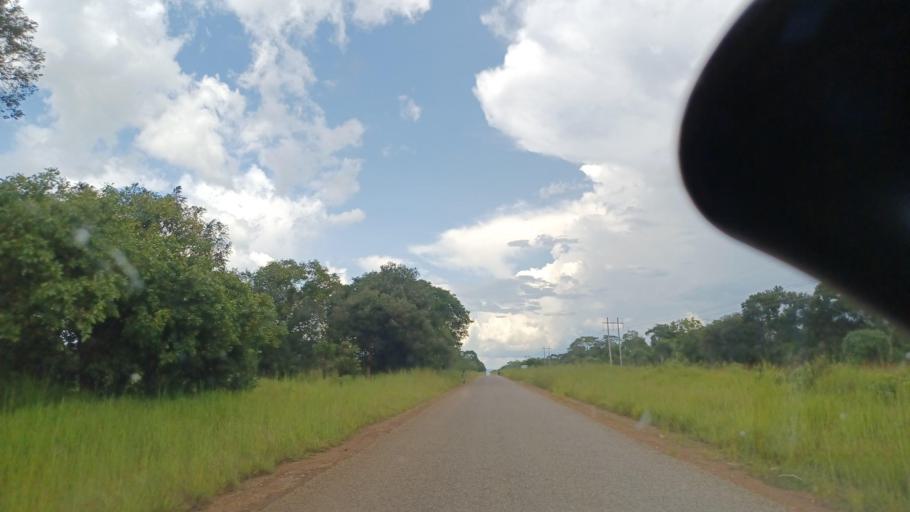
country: ZM
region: North-Western
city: Kasempa
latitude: -12.8003
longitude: 26.0188
